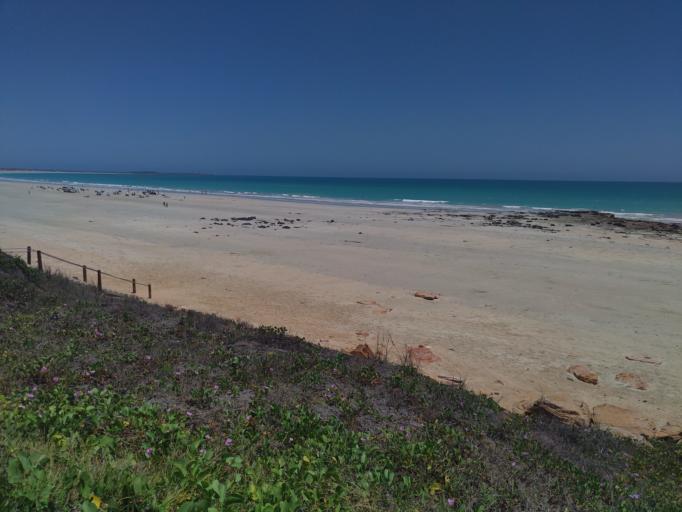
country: AU
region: Western Australia
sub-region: Broome
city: Broome
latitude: -17.9287
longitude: 122.2101
